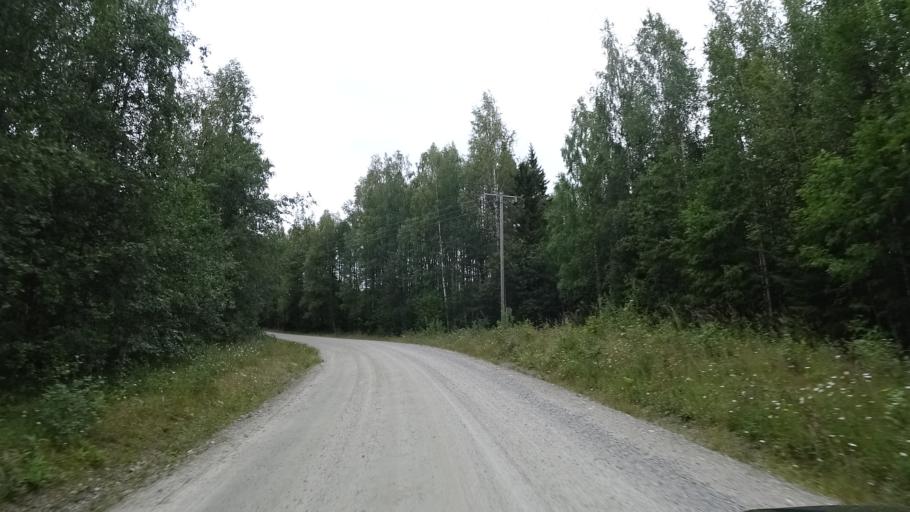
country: FI
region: North Karelia
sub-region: Joensuu
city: Eno
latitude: 63.1757
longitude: 30.5524
